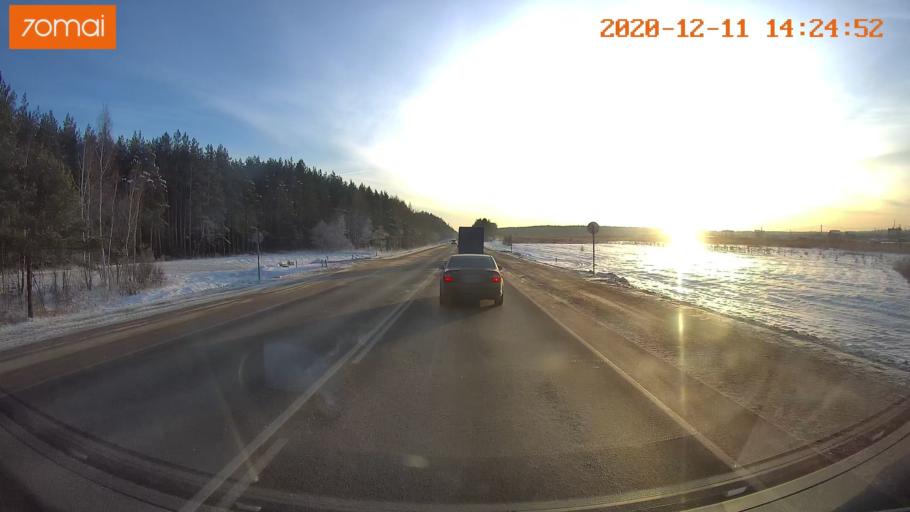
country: RU
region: Kostroma
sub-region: Kostromskoy Rayon
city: Kostroma
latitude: 57.7159
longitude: 40.8942
